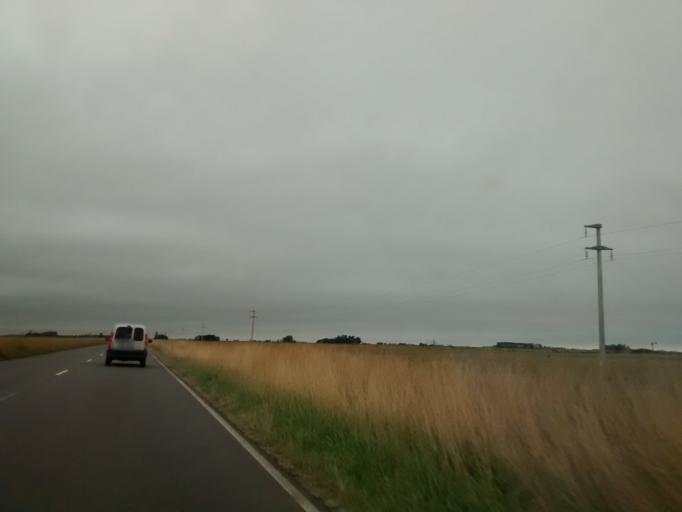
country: AR
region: Buenos Aires
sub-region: Partido de Ayacucho
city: Ayacucho
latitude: -37.0184
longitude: -58.5383
